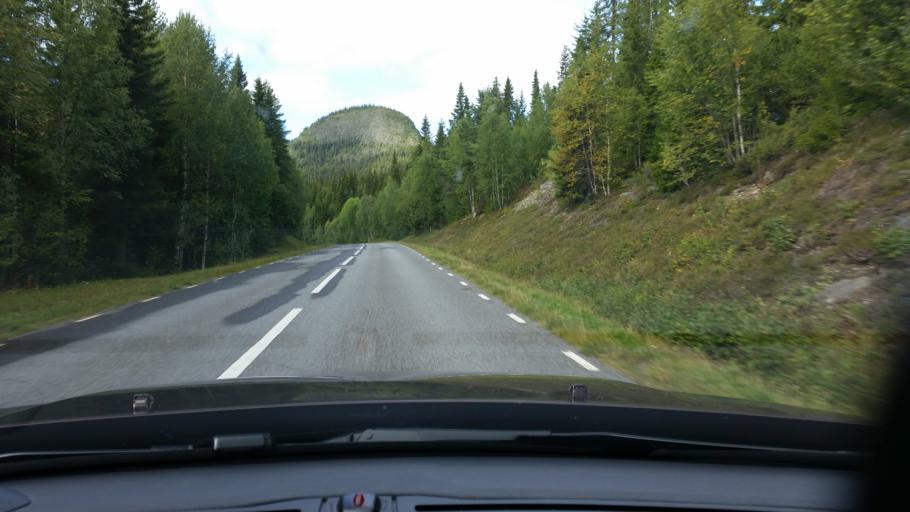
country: NO
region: Nord-Trondelag
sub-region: Lierne
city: Sandvika
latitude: 64.3787
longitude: 14.6362
